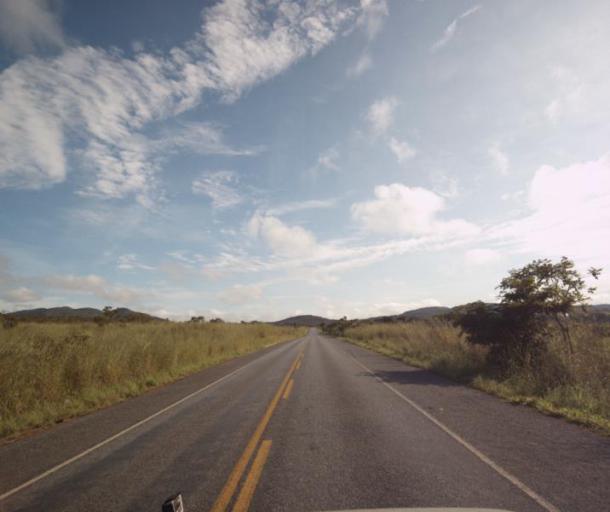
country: BR
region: Goias
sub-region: Pirenopolis
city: Pirenopolis
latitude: -15.5505
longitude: -48.6229
